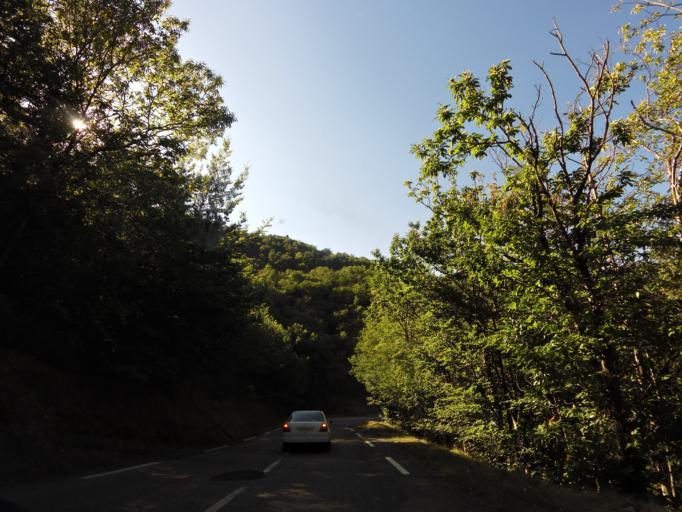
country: FR
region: Languedoc-Roussillon
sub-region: Departement du Gard
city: Valleraugue
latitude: 44.0898
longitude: 3.5773
